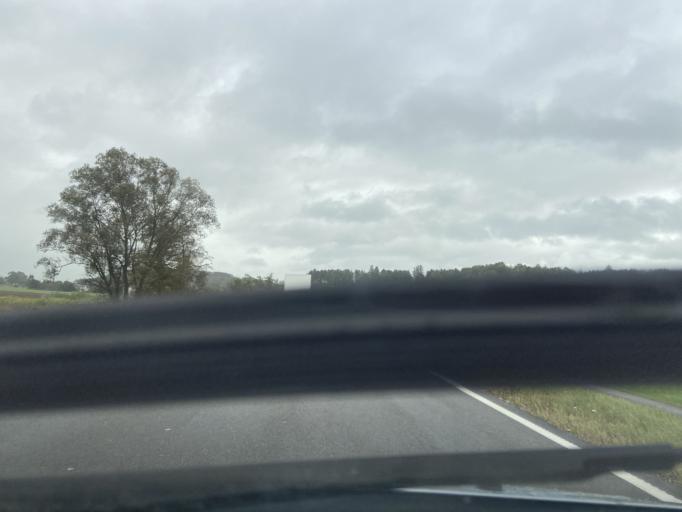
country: DE
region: Baden-Wuerttemberg
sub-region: Tuebingen Region
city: Messkirch
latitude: 48.0015
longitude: 9.1826
